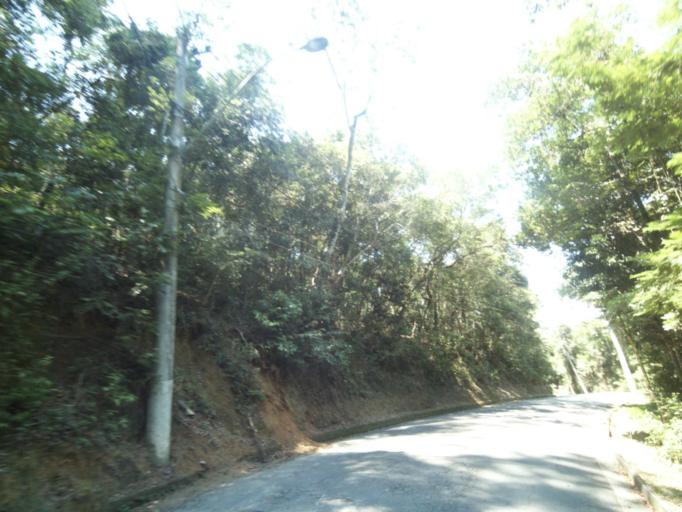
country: BR
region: Rio de Janeiro
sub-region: Niteroi
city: Niteroi
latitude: -22.9275
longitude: -43.0850
